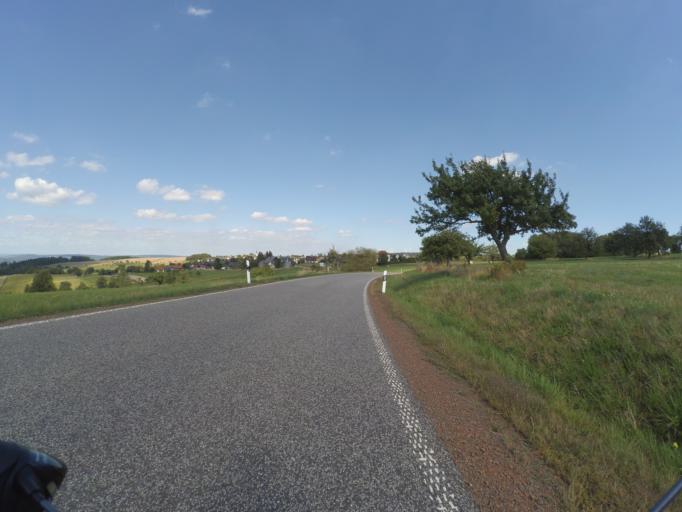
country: DE
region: Rheinland-Pfalz
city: Heidenburg
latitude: 49.7925
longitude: 6.9138
